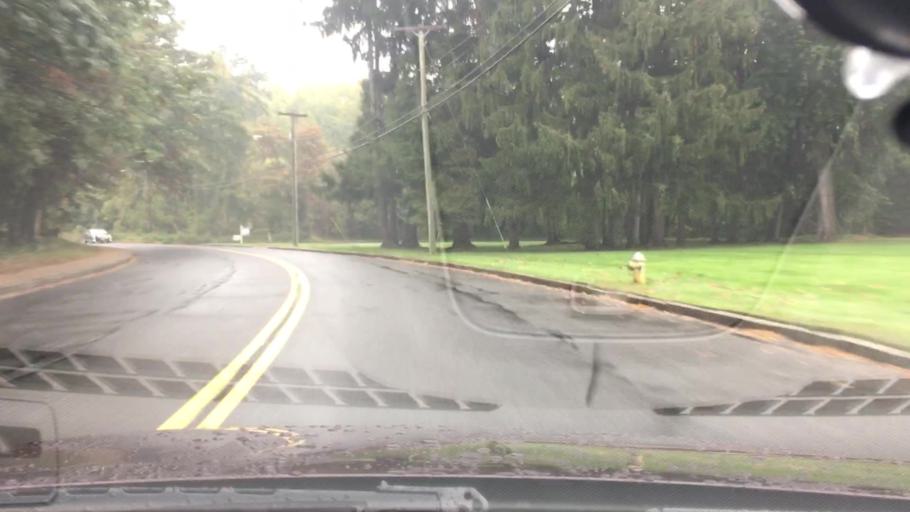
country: US
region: Massachusetts
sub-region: Hampden County
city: Longmeadow
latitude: 42.0725
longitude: -72.5509
